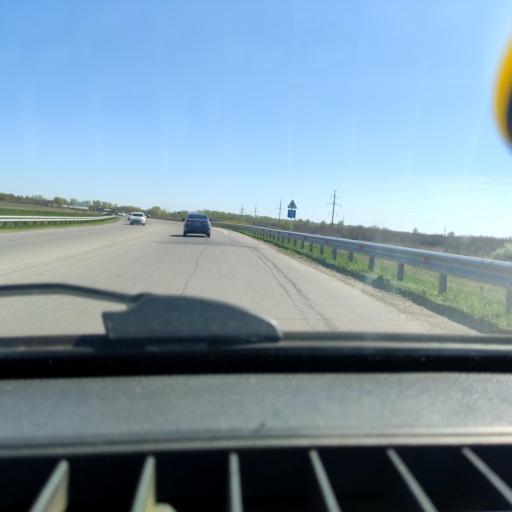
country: RU
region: Samara
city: Tol'yatti
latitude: 53.6699
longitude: 49.4147
